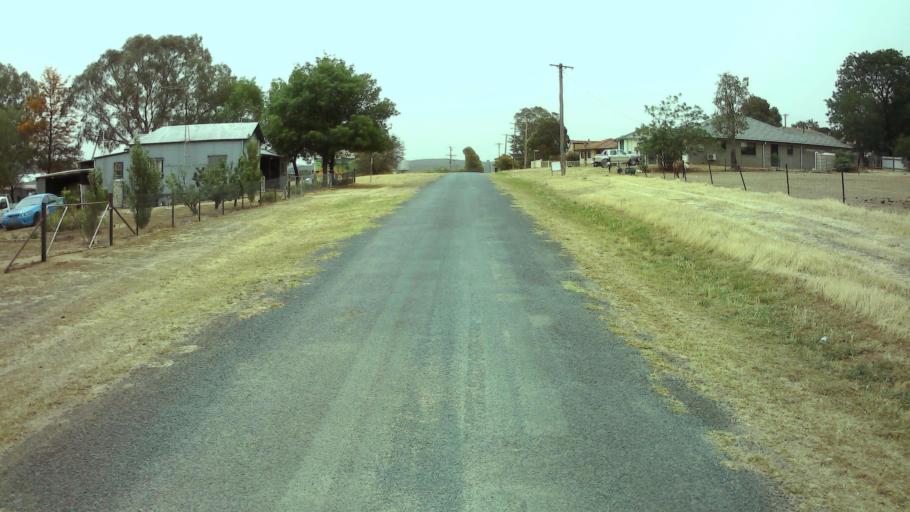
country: AU
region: New South Wales
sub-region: Weddin
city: Grenfell
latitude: -33.9025
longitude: 148.1547
